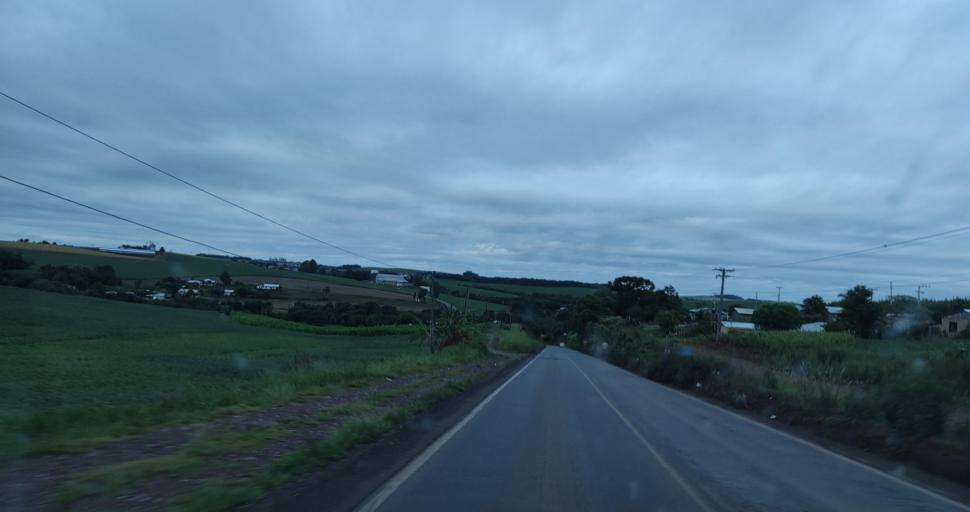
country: BR
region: Santa Catarina
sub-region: Xanxere
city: Xanxere
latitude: -26.7449
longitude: -52.3975
